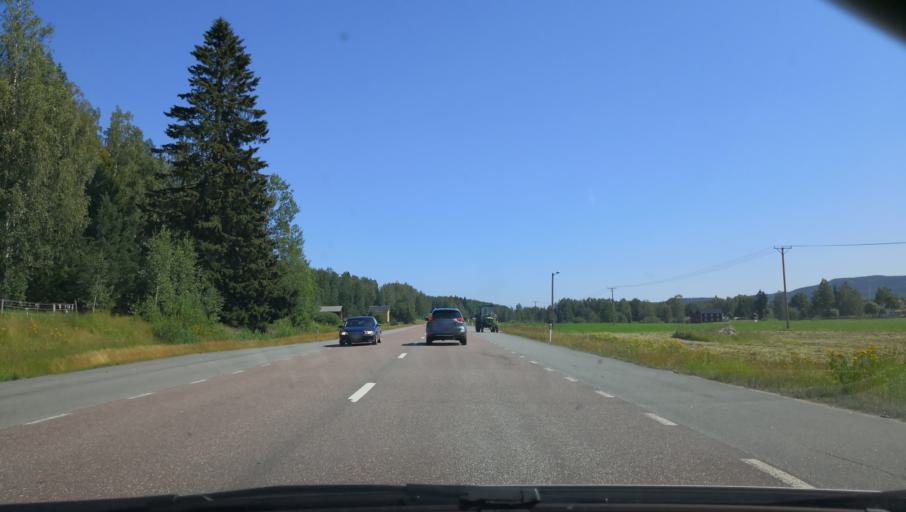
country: SE
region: Gaevleborg
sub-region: Ovanakers Kommun
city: Alfta
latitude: 61.3330
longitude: 16.2296
